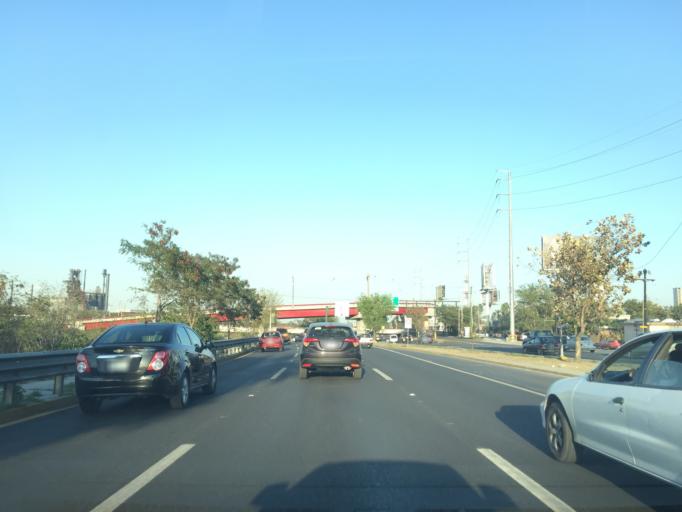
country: MX
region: Nuevo Leon
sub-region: Monterrey
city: Monterrey
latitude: 25.6708
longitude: -100.2882
